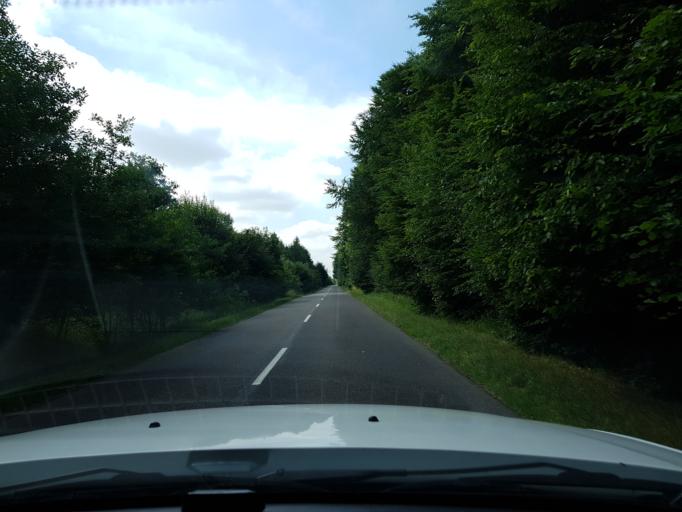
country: PL
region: West Pomeranian Voivodeship
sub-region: Powiat gryfinski
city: Banie
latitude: 53.0074
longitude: 14.7227
